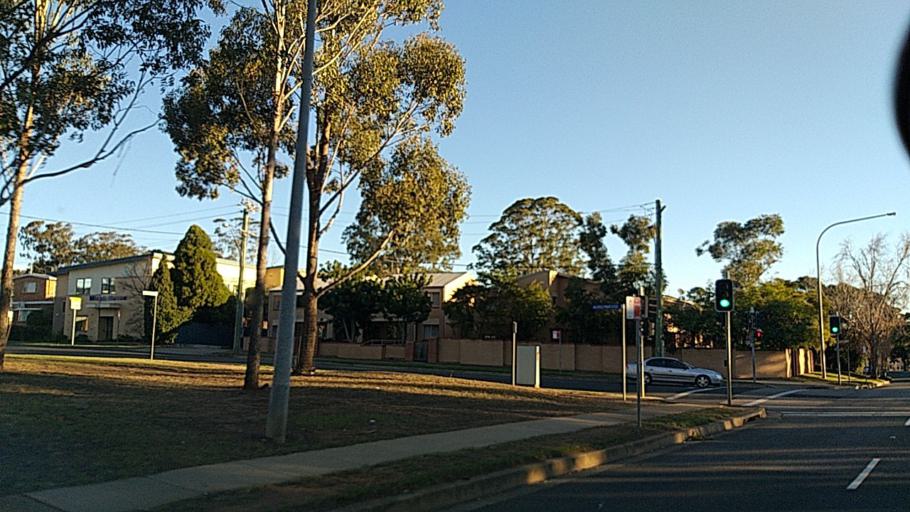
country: AU
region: New South Wales
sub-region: Campbelltown Municipality
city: Campbelltown
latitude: -34.0678
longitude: 150.8174
